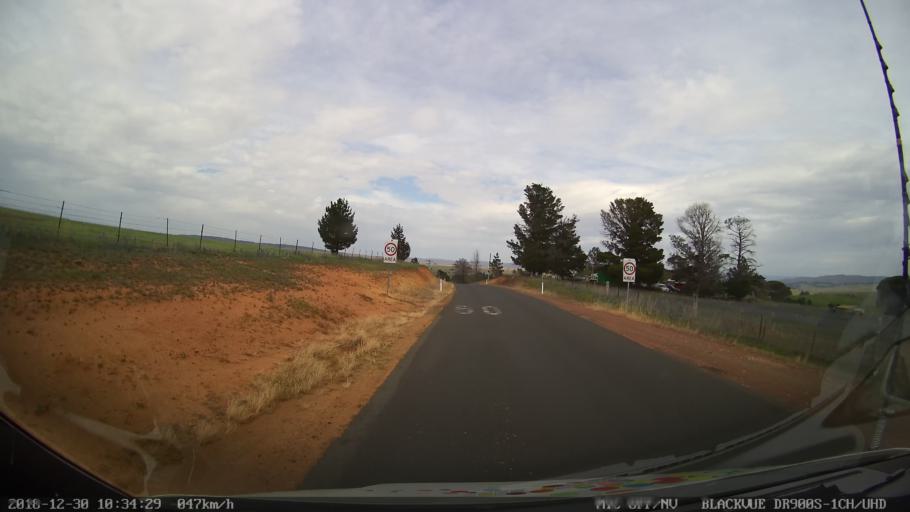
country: AU
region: New South Wales
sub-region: Snowy River
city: Berridale
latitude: -36.5010
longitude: 148.8403
